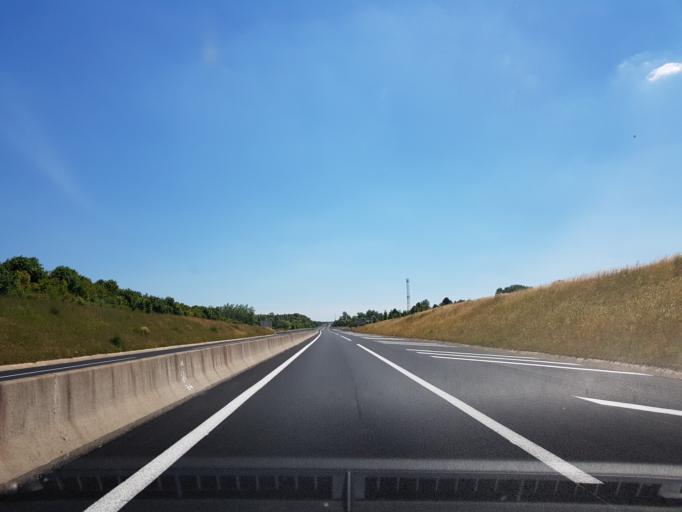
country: FR
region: Picardie
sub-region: Departement de la Somme
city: Nesle
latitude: 49.8350
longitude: 2.9197
